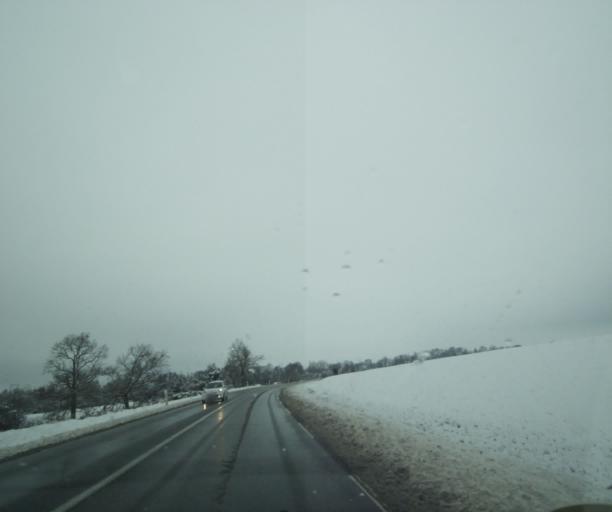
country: FR
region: Champagne-Ardenne
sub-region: Departement de la Haute-Marne
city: Montier-en-Der
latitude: 48.5102
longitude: 4.8017
